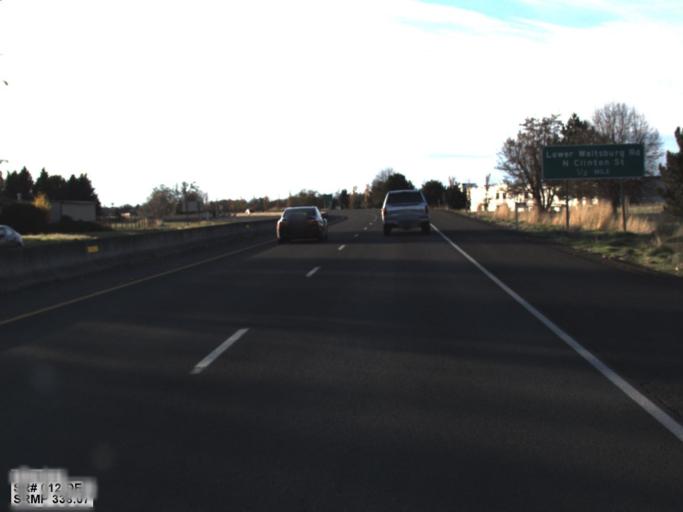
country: US
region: Washington
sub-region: Walla Walla County
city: Walla Walla
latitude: 46.0829
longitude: -118.3180
